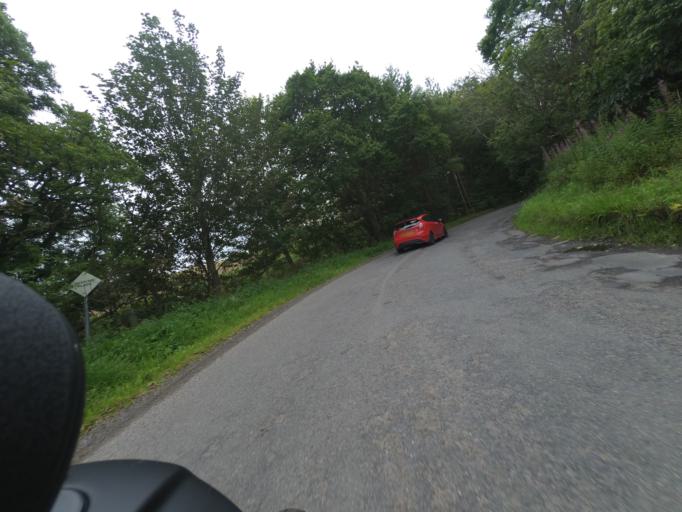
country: GB
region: Scotland
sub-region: Highland
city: Inverness
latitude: 57.5112
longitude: -4.2581
